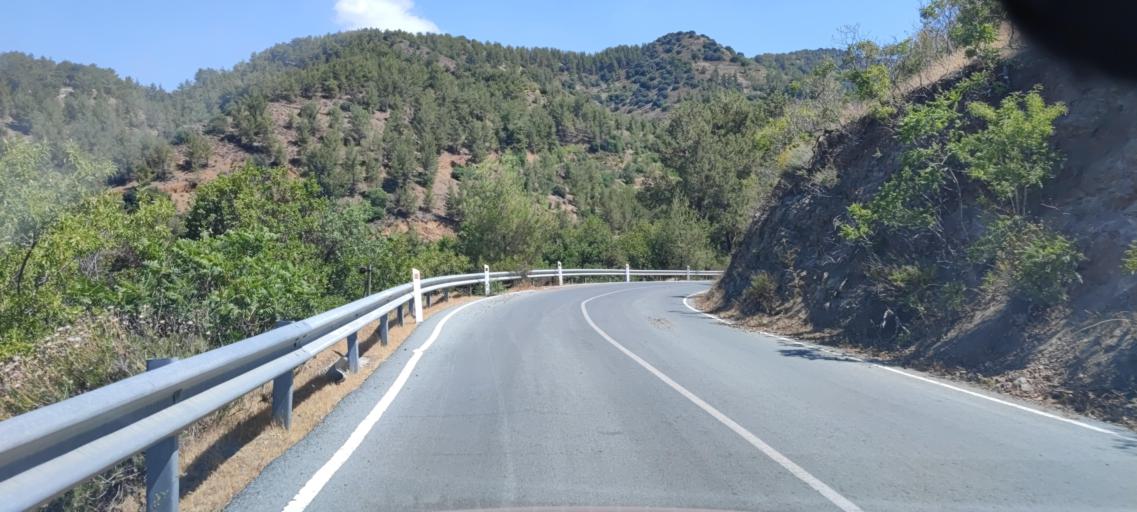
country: CY
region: Lefkosia
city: Kakopetria
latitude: 34.9269
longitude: 32.8056
